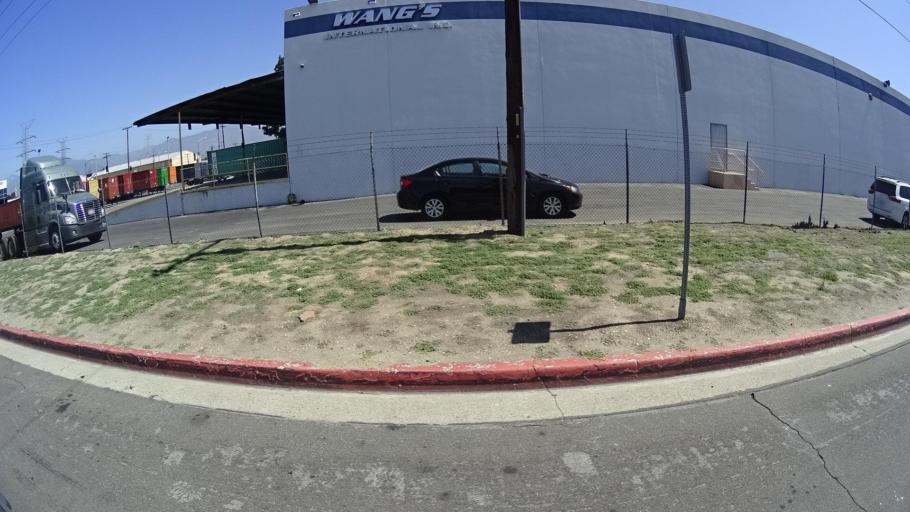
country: US
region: California
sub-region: Los Angeles County
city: Avocado Heights
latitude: 34.0536
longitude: -118.0008
